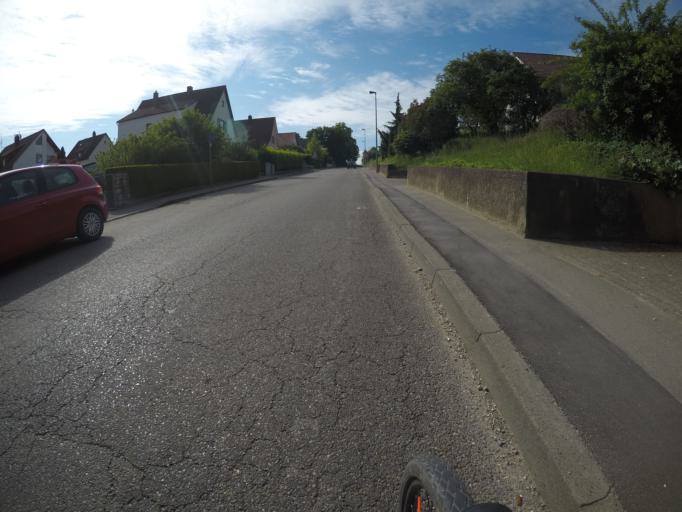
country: DE
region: Baden-Wuerttemberg
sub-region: Regierungsbezirk Stuttgart
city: Neuhausen auf den Fildern
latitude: 48.6761
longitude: 9.2824
